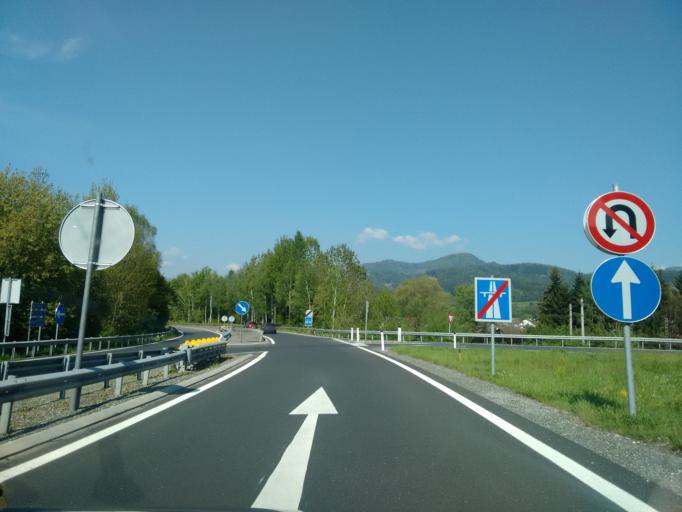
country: AT
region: Styria
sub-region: Politischer Bezirk Bruck-Muerzzuschlag
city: Frauenberg
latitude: 47.4512
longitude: 15.3225
